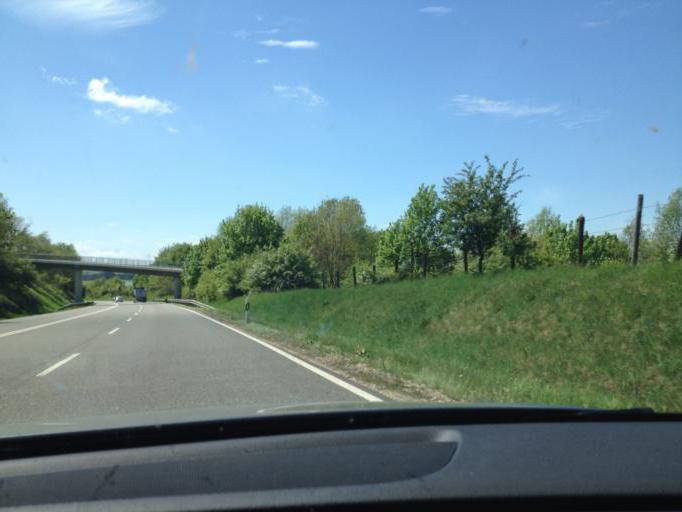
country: DE
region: North Rhine-Westphalia
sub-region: Regierungsbezirk Koln
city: Blankenheim
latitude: 50.4493
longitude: 6.6300
